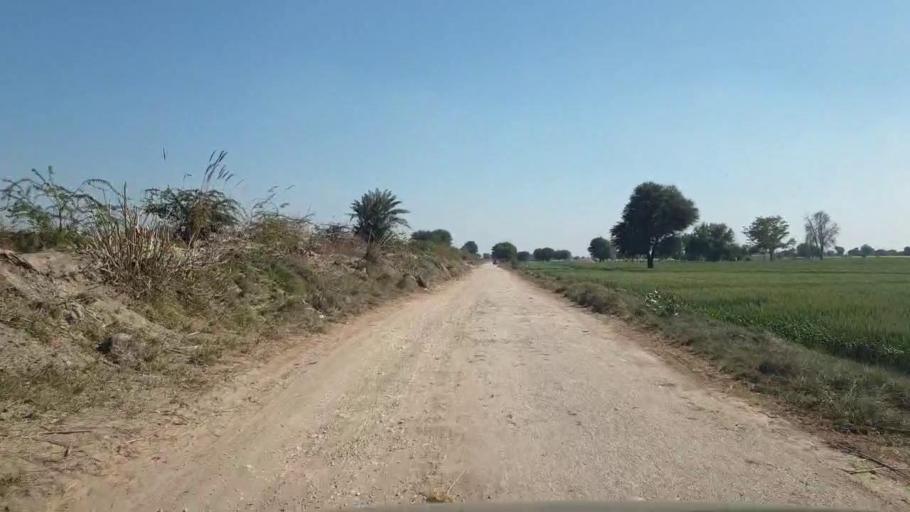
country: PK
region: Sindh
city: Shahpur Chakar
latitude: 26.1461
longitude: 68.6463
